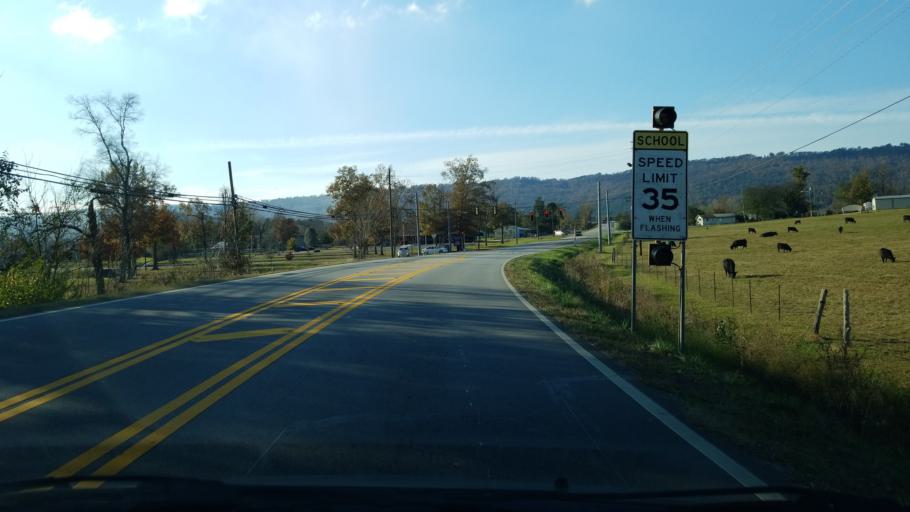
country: US
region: Georgia
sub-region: Dade County
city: Trenton
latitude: 34.8630
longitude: -85.5043
